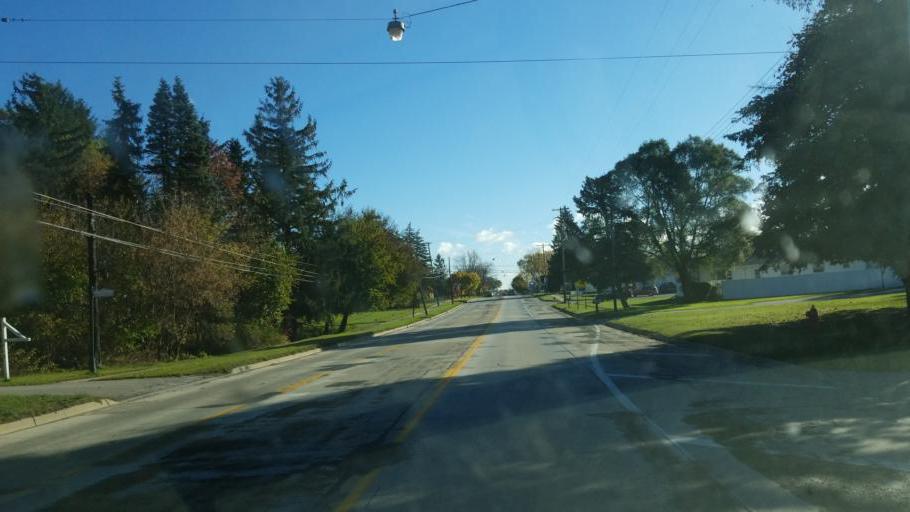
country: US
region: Michigan
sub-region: Montcalm County
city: Edmore
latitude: 43.4081
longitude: -85.0492
